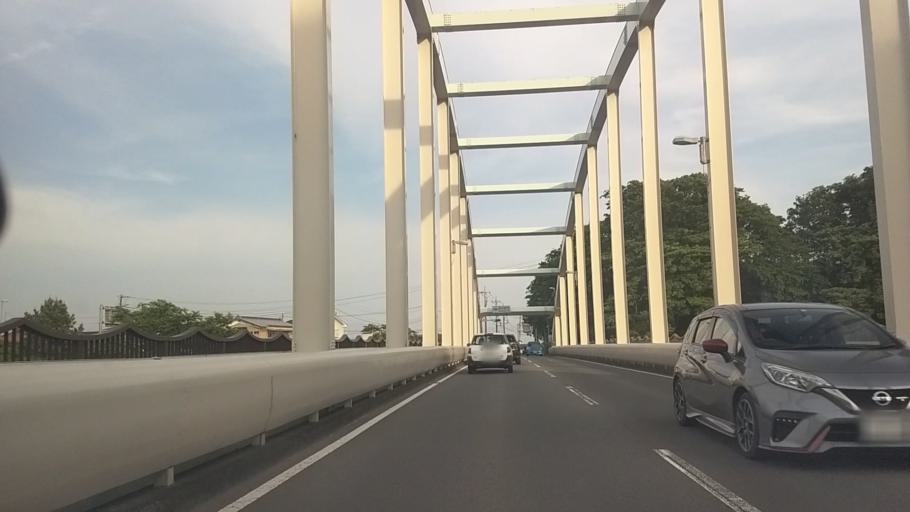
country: JP
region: Kanagawa
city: Odawara
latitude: 35.3473
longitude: 139.0969
